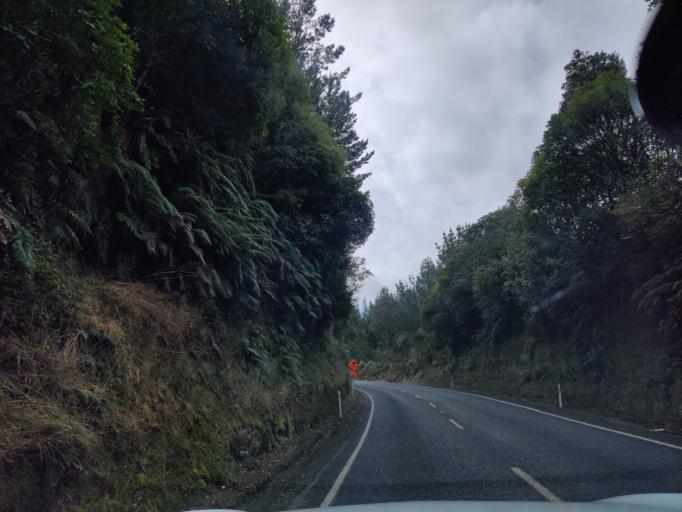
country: NZ
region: Waikato
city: Turangi
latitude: -38.7519
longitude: 175.6762
